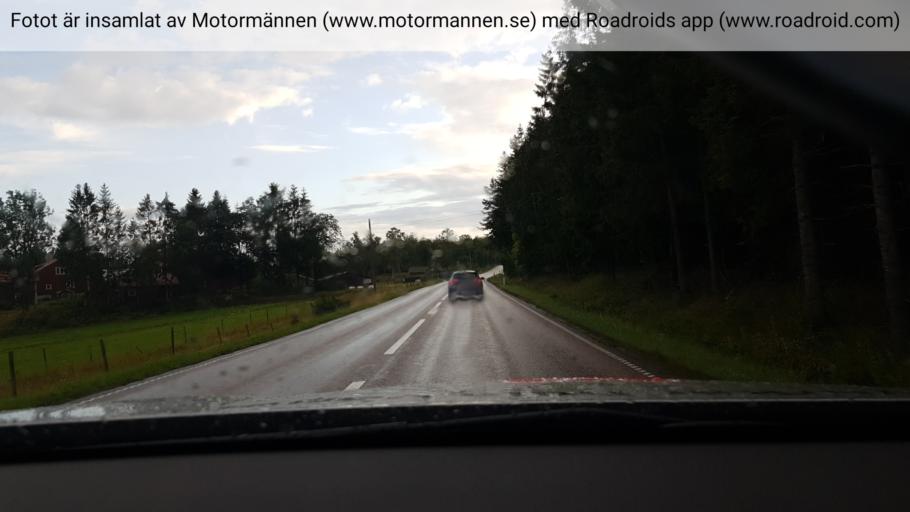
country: SE
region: Stockholm
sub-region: Norrtalje Kommun
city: Norrtalje
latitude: 59.8745
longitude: 18.7009
